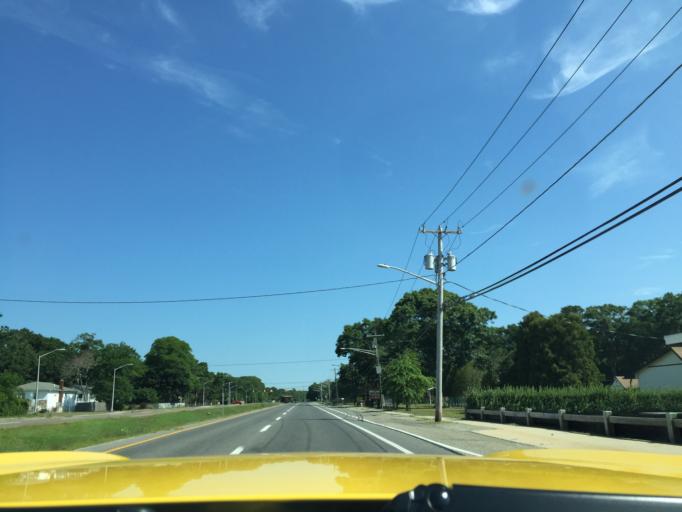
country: US
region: New York
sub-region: Suffolk County
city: Mastic Beach
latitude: 40.7507
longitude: -72.8716
